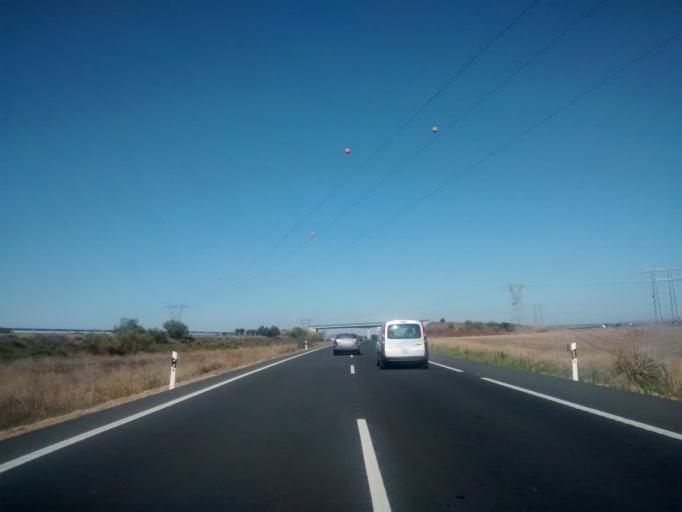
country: ES
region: Andalusia
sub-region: Provincia de Huelva
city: San Juan del Puerto
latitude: 37.3131
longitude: -6.8823
